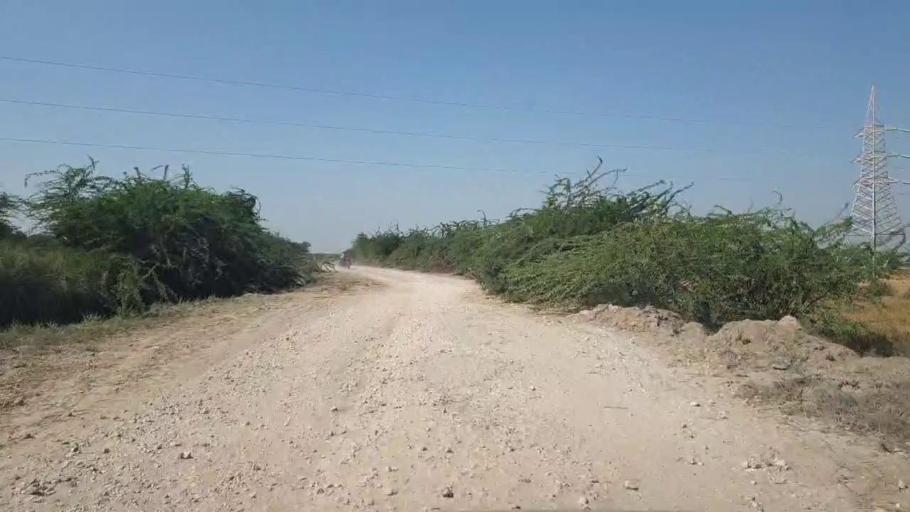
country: PK
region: Sindh
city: Talhar
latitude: 24.8346
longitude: 68.8105
